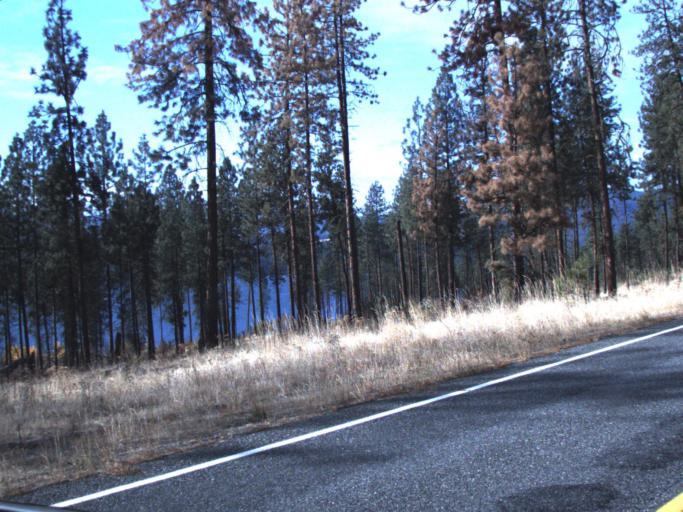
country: US
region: Washington
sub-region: Stevens County
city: Kettle Falls
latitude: 48.2896
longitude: -118.1409
